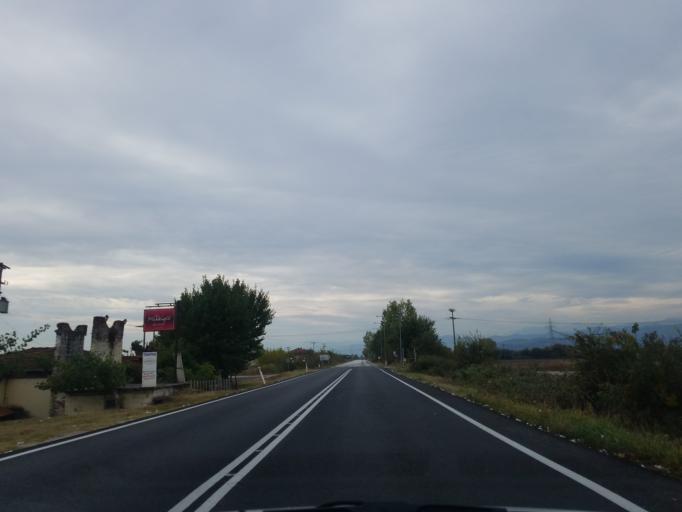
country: GR
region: Thessaly
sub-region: Nomos Kardhitsas
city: Agnantero
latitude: 39.4952
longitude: 21.8385
